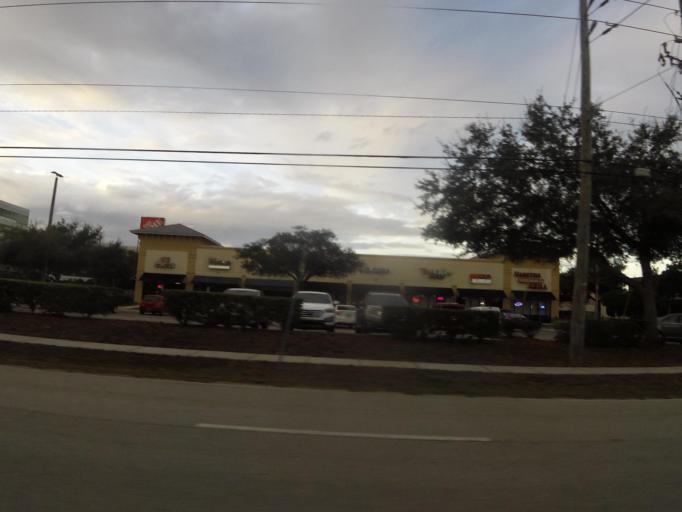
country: US
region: Florida
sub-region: Duval County
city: Jacksonville
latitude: 30.3264
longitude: -81.5510
